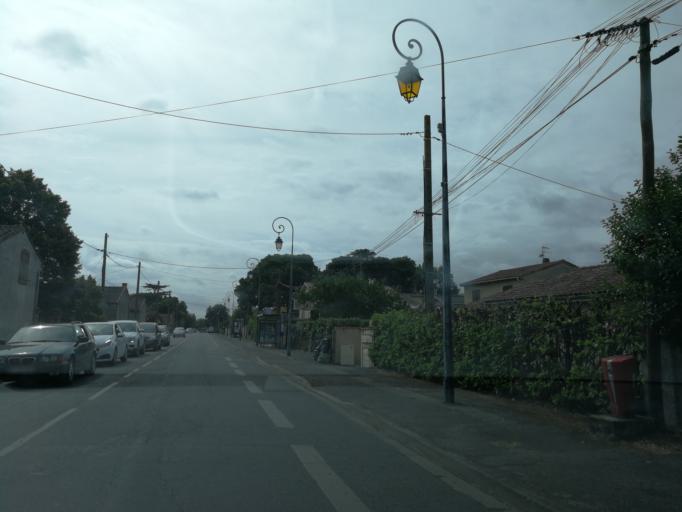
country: FR
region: Midi-Pyrenees
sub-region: Departement de la Haute-Garonne
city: Aucamville
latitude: 43.6735
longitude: 1.4258
